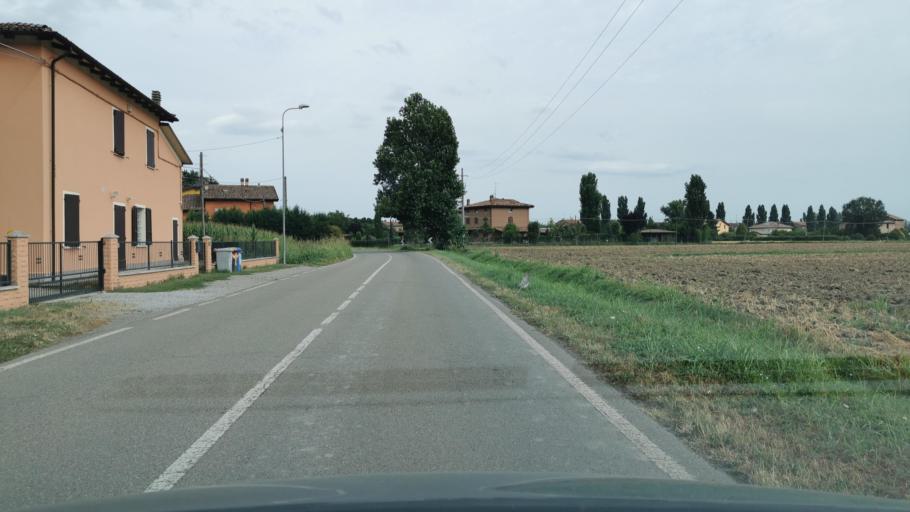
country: IT
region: Emilia-Romagna
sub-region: Provincia di Modena
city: Villanova
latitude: 44.7048
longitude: 10.9046
